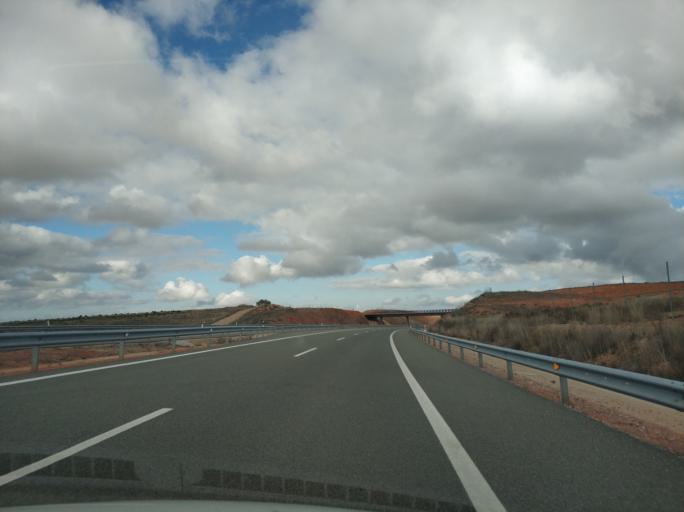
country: ES
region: Castille and Leon
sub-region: Provincia de Soria
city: Yelo
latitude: 41.2383
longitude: -2.4794
